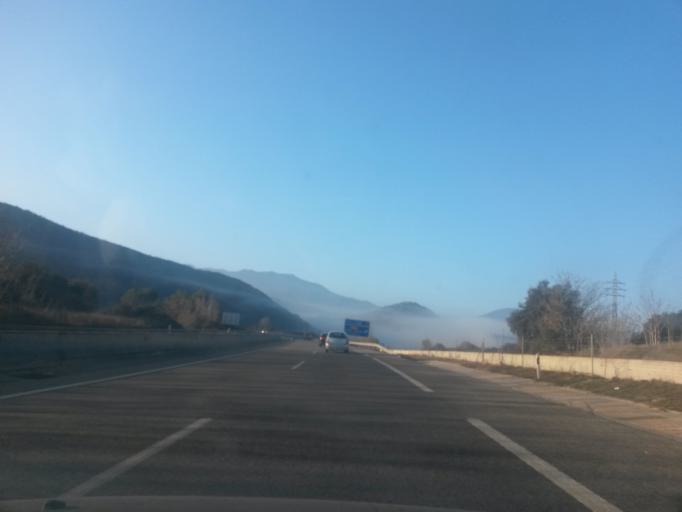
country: ES
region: Catalonia
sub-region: Provincia de Girona
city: Argelaguer
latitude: 42.2154
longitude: 2.6290
